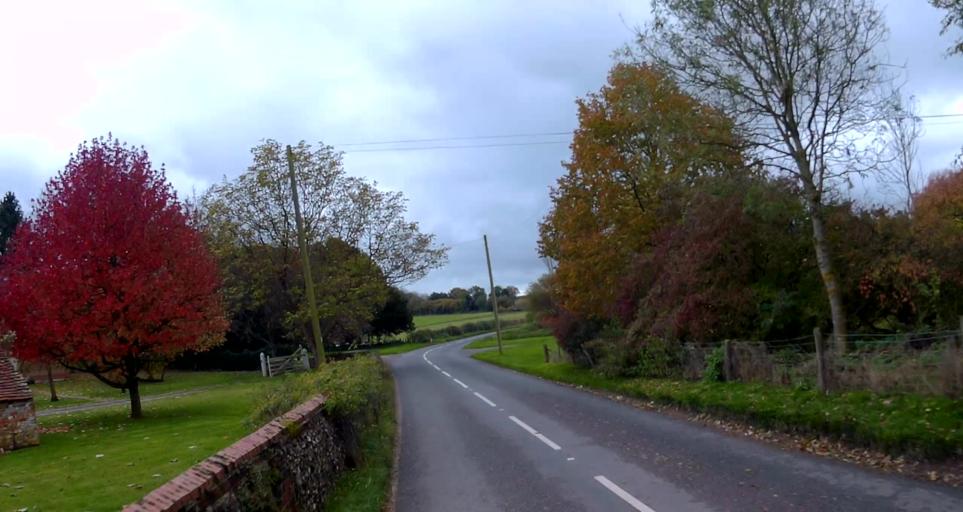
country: GB
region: England
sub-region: Hampshire
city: Four Marks
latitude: 51.1571
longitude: -1.1549
